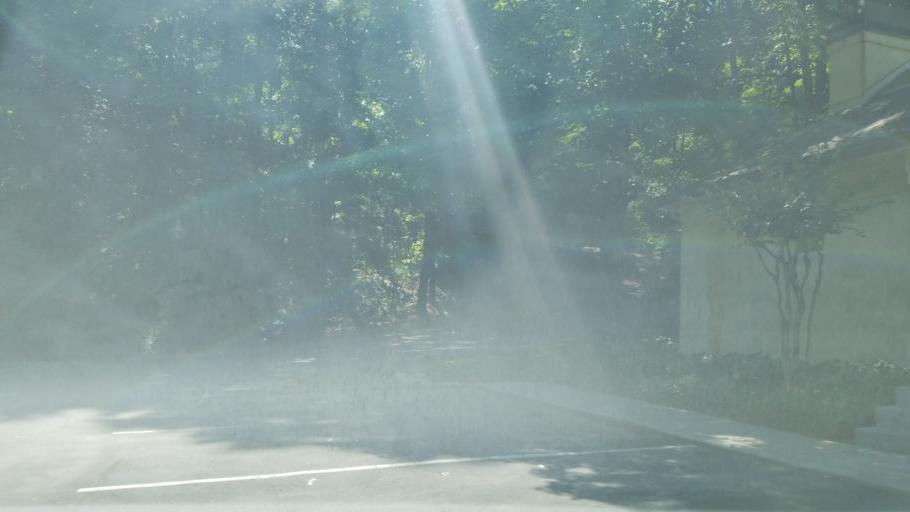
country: US
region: Georgia
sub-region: Cobb County
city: Vinings
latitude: 33.8964
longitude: -84.4748
